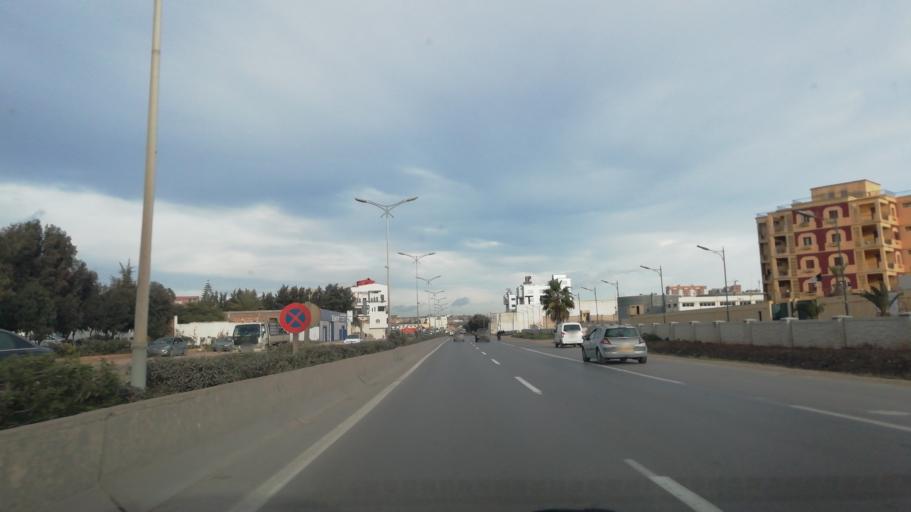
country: DZ
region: Oran
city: Bir el Djir
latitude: 35.7155
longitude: -0.5709
